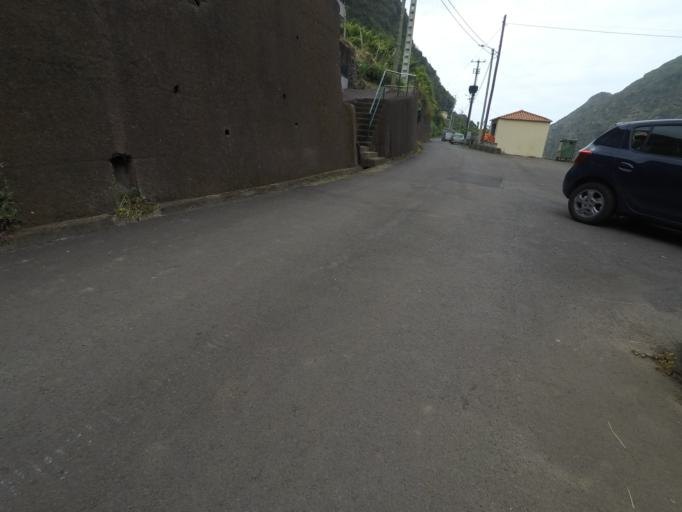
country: PT
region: Madeira
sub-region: Sao Vicente
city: Sao Vicente
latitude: 32.8106
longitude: -16.9665
